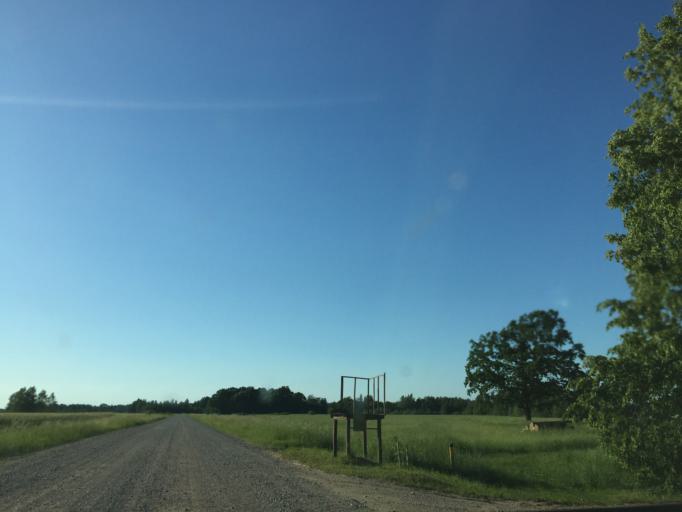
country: LV
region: Kandava
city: Kandava
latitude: 56.8434
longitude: 22.7093
